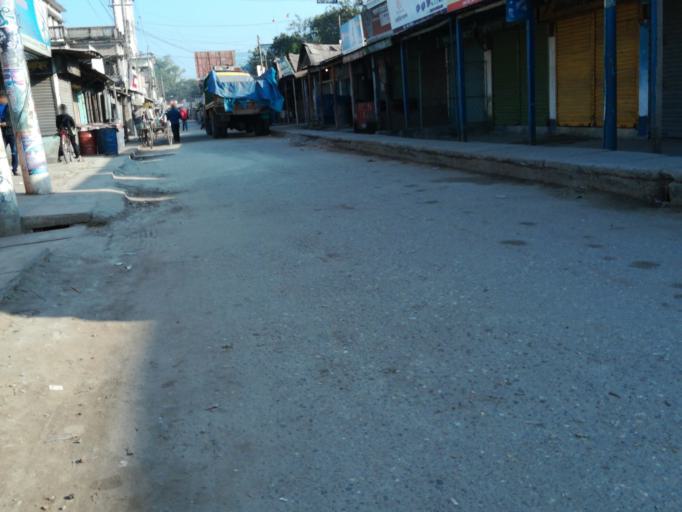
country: BD
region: Rangpur Division
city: Nageswari
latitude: 25.8135
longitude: 89.6485
